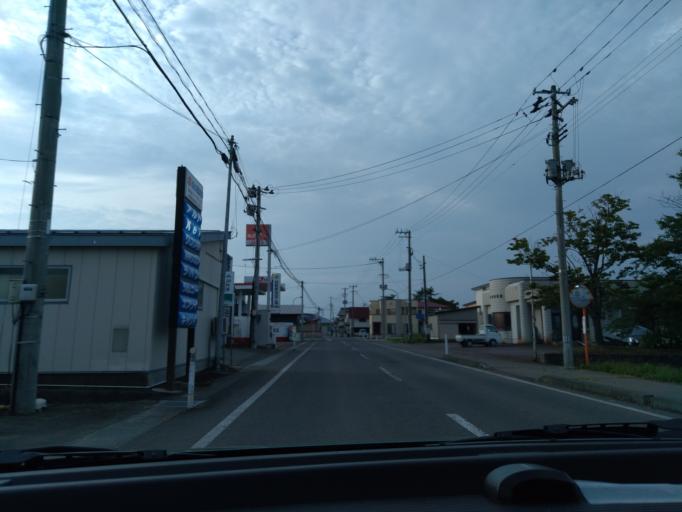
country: JP
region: Akita
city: Omagari
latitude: 39.4031
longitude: 140.5181
